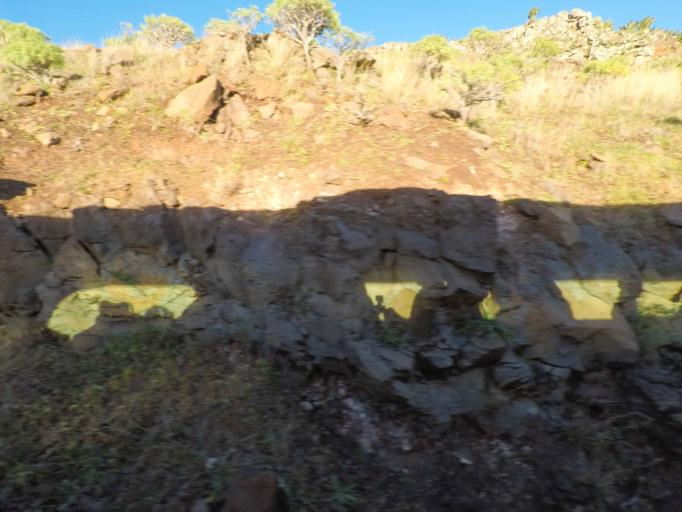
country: ES
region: Canary Islands
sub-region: Provincia de Santa Cruz de Tenerife
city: San Sebastian de la Gomera
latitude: 28.0977
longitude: -17.1618
